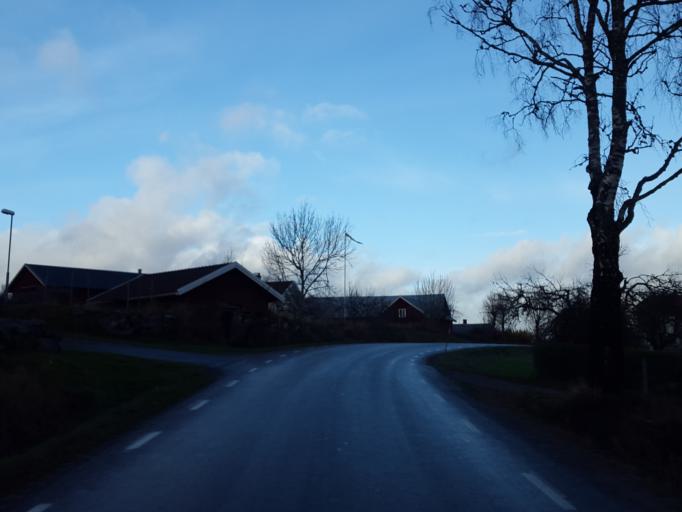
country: SE
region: Vaestra Goetaland
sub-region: Vargarda Kommun
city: Jonstorp
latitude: 57.9653
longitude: 12.7273
